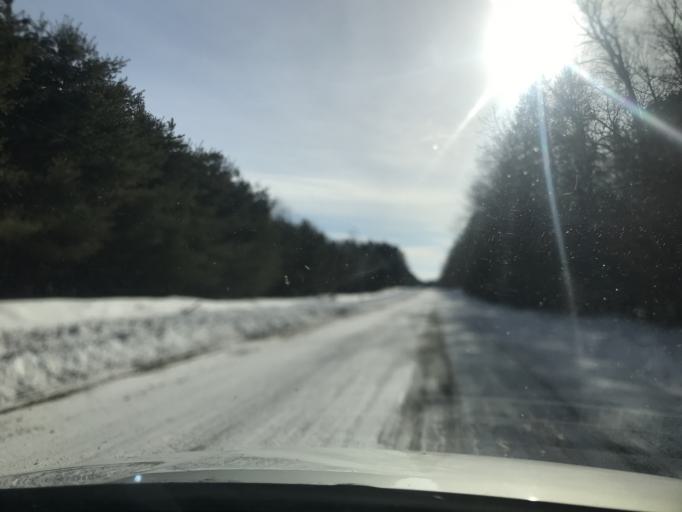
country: US
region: Wisconsin
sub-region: Oconto County
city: Gillett
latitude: 45.1292
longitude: -88.2497
